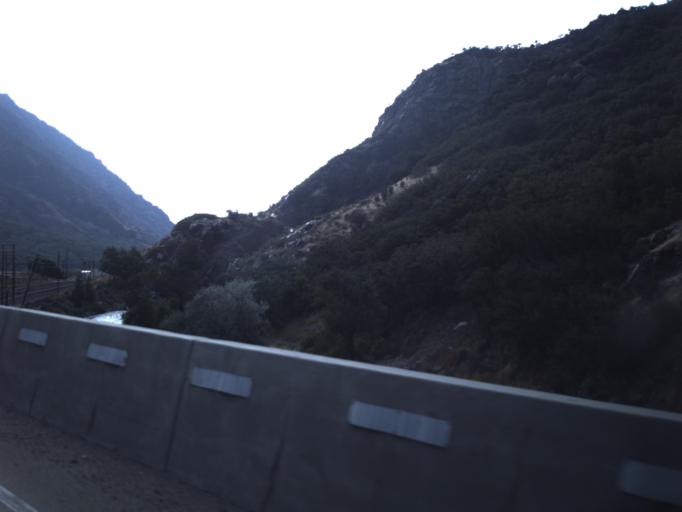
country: US
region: Utah
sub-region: Morgan County
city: Mountain Green
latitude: 41.1391
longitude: -111.8554
